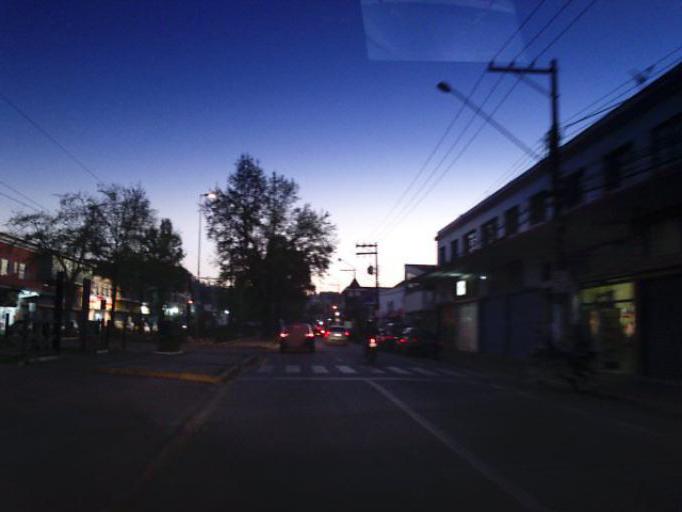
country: BR
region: Sao Paulo
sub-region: Campos Do Jordao
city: Campos do Jordao
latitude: -22.7399
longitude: -45.5937
